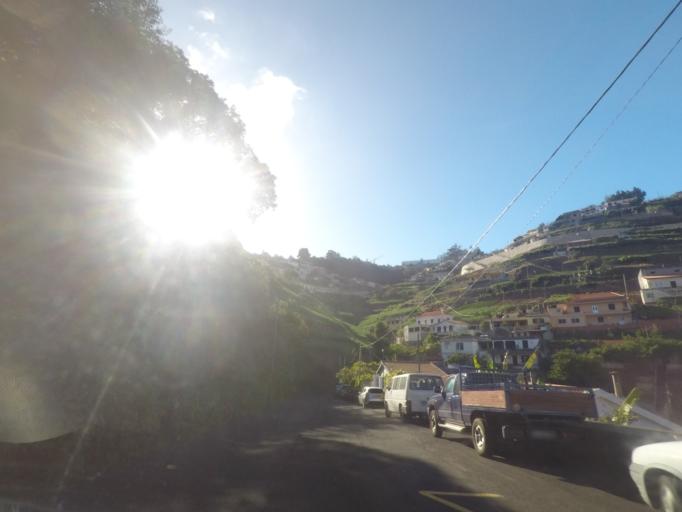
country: PT
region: Madeira
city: Camara de Lobos
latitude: 32.6653
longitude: -16.9911
